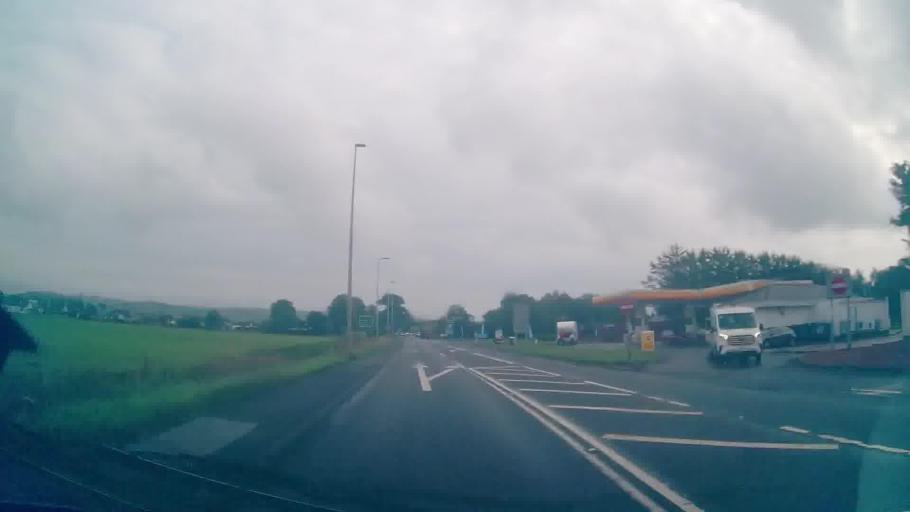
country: GB
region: Scotland
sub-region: Dumfries and Galloway
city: Locharbriggs
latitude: 55.0687
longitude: -3.5554
